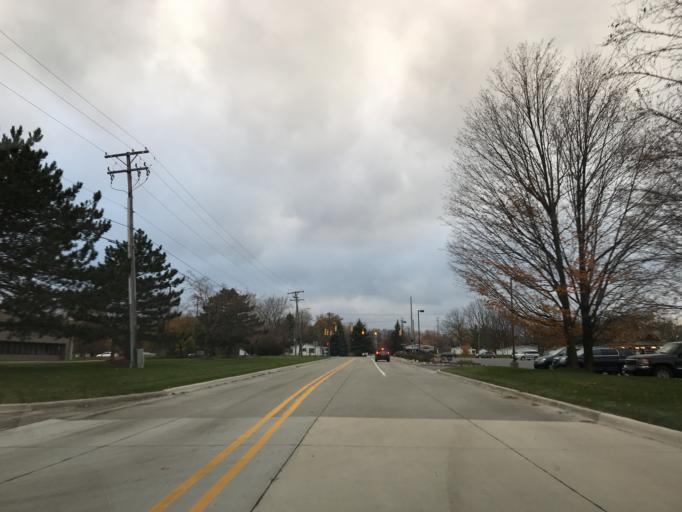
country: US
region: Michigan
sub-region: Oakland County
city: Novi
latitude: 42.4899
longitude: -83.4340
